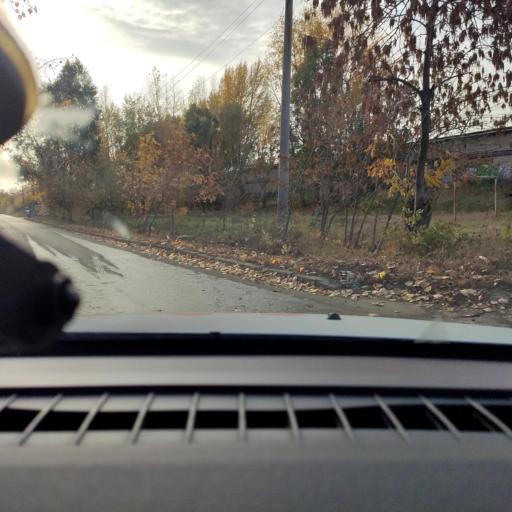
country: RU
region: Samara
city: Samara
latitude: 53.1231
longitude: 50.0835
